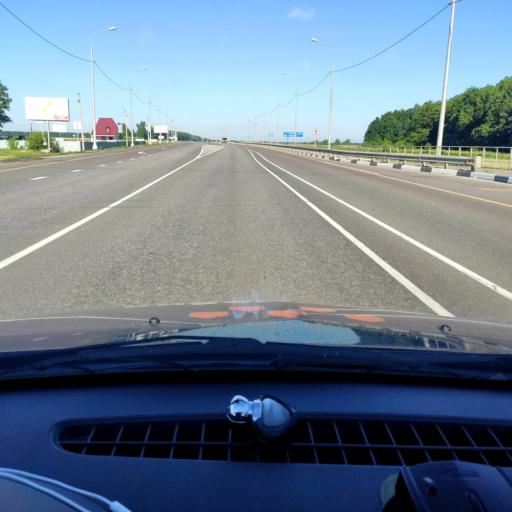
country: RU
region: Orjol
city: Pokrovskoye
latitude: 52.6222
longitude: 36.7781
